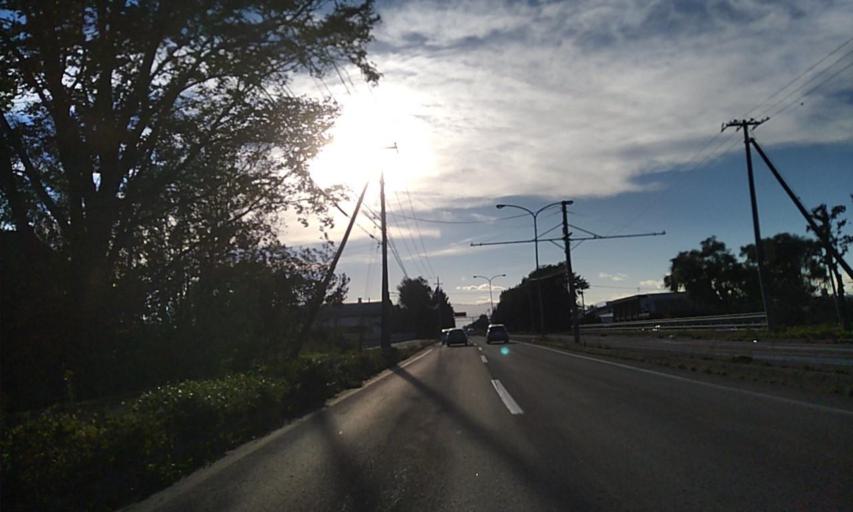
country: JP
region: Hokkaido
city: Obihiro
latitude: 42.9277
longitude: 143.1432
